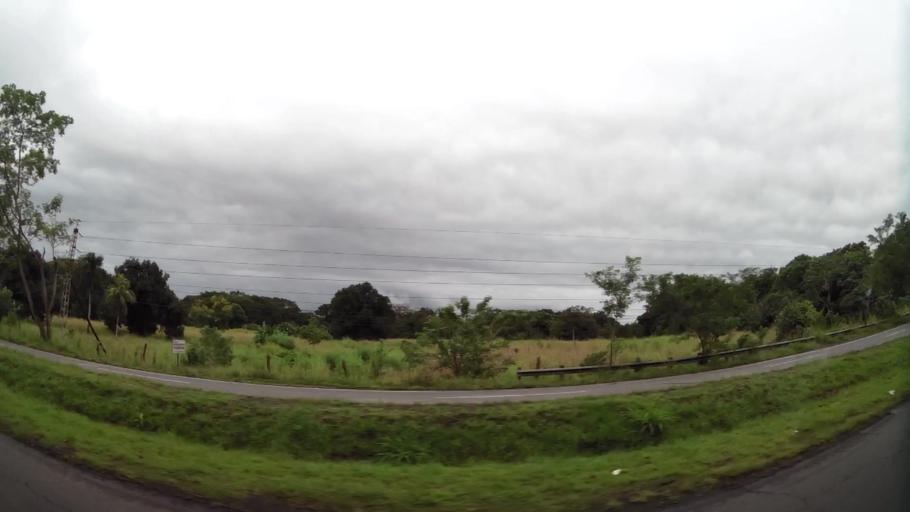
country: PA
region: Chiriqui
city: Tijera
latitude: 8.4724
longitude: -82.5408
